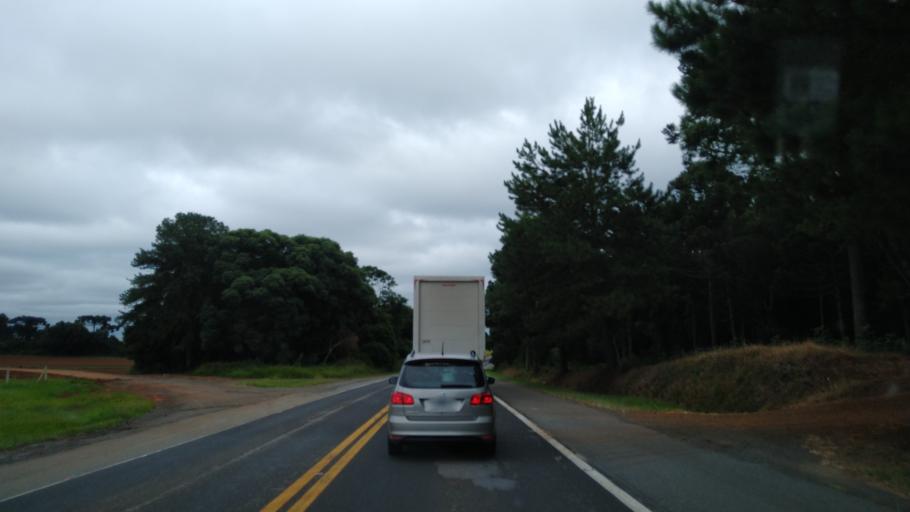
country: BR
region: Santa Catarina
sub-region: Tres Barras
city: Tres Barras
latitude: -26.1689
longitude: -50.0982
